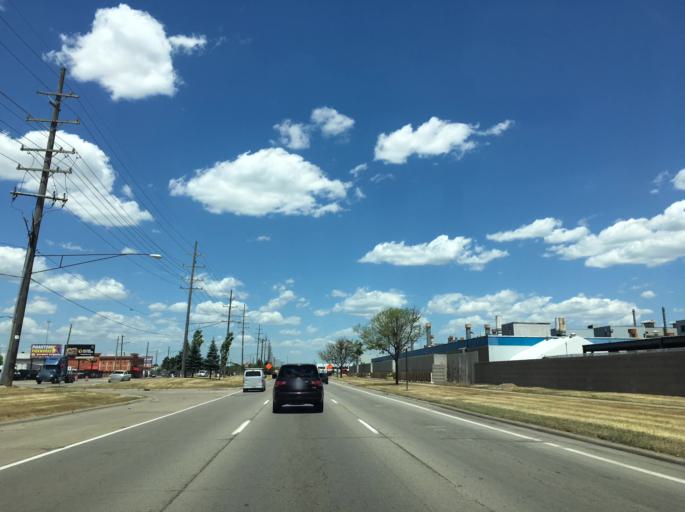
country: US
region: Michigan
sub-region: Macomb County
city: Warren
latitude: 42.4534
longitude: -83.0442
